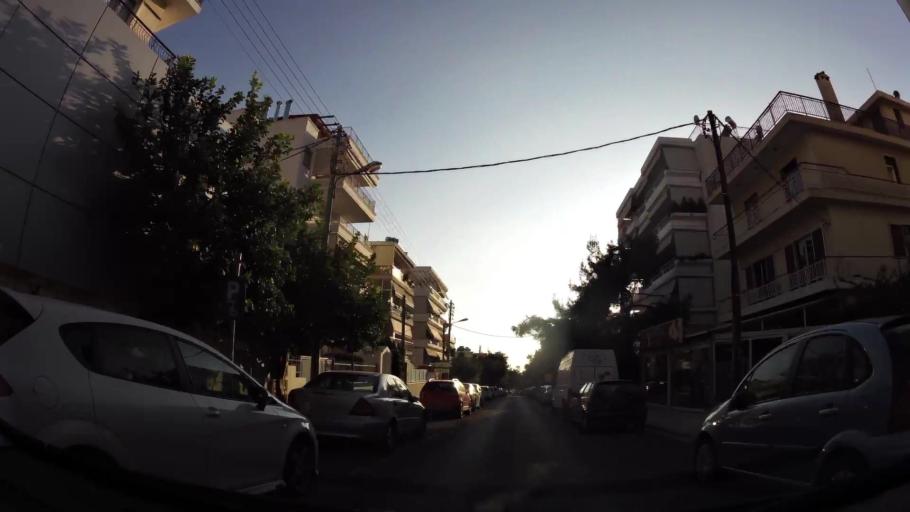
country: GR
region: Attica
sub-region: Nomarchia Athinas
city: Argyroupoli
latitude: 37.9005
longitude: 23.7710
